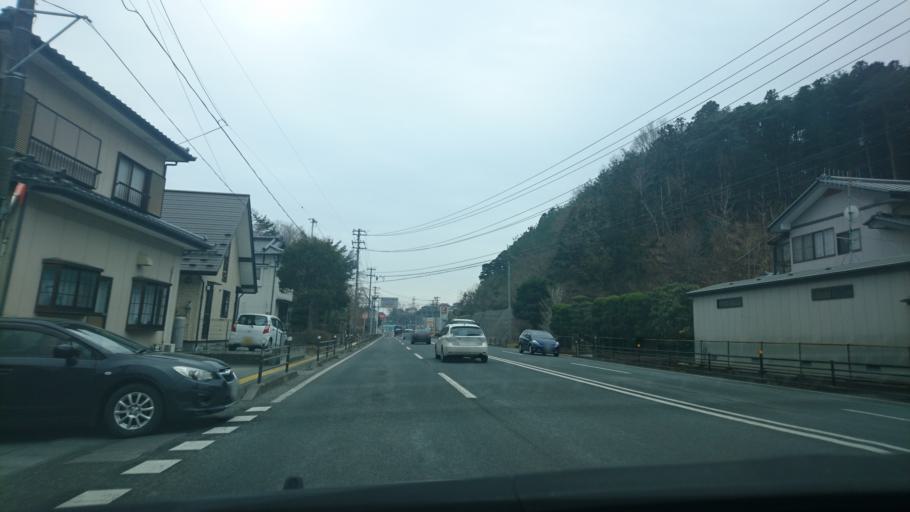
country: JP
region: Iwate
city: Ofunato
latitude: 39.0840
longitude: 141.7080
